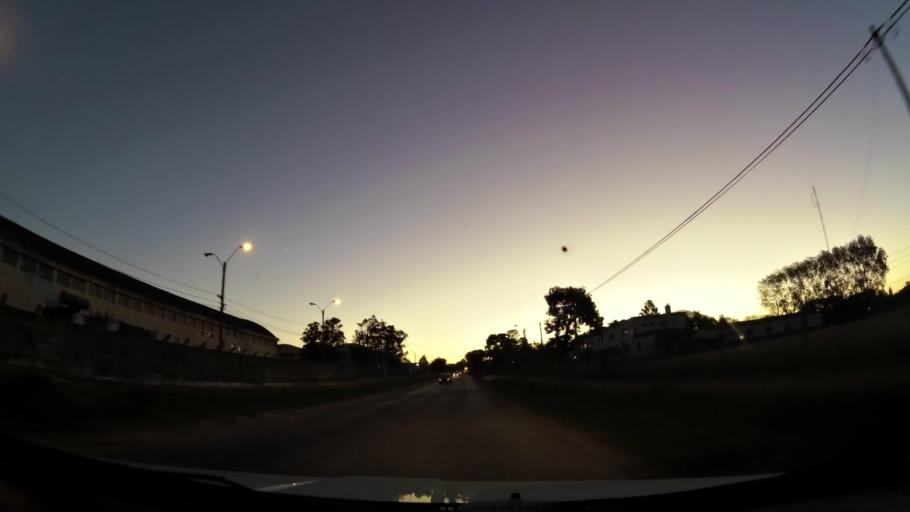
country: UY
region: Montevideo
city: Montevideo
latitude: -34.8309
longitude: -56.1869
